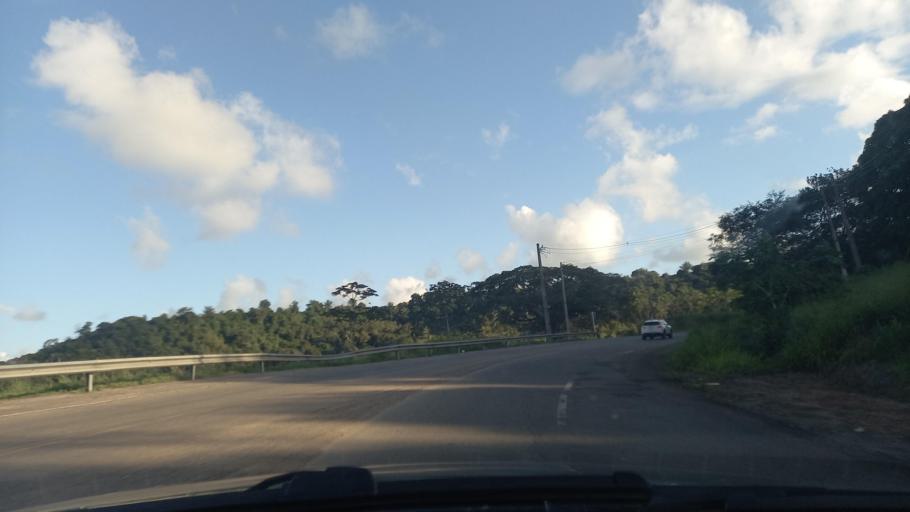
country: BR
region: Alagoas
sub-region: Sao Miguel Dos Campos
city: Sao Miguel dos Campos
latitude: -9.8191
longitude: -36.2191
